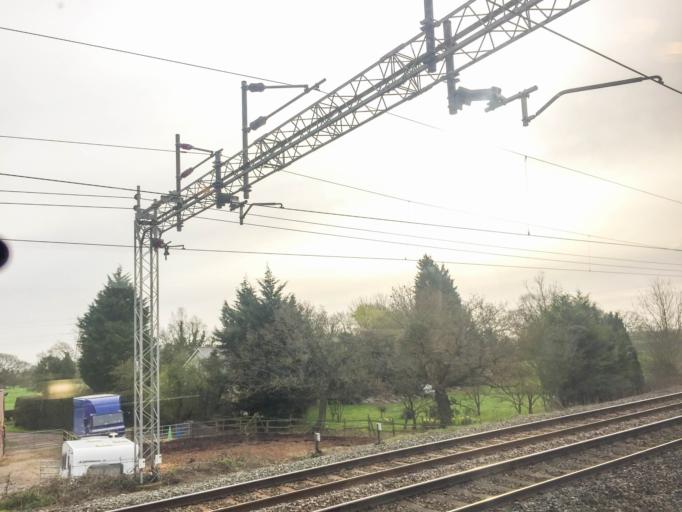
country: GB
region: England
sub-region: Cheshire West and Chester
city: Winsford
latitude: 53.1803
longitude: -2.4853
